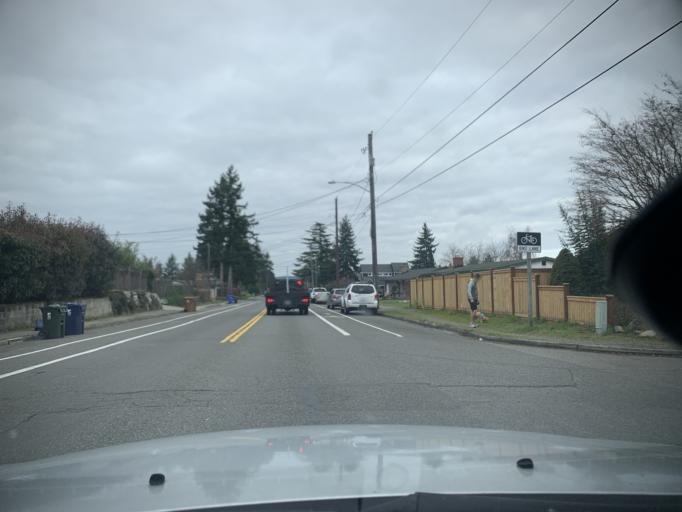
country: US
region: Washington
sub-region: Pierce County
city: Fircrest
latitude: 47.2931
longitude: -122.5210
